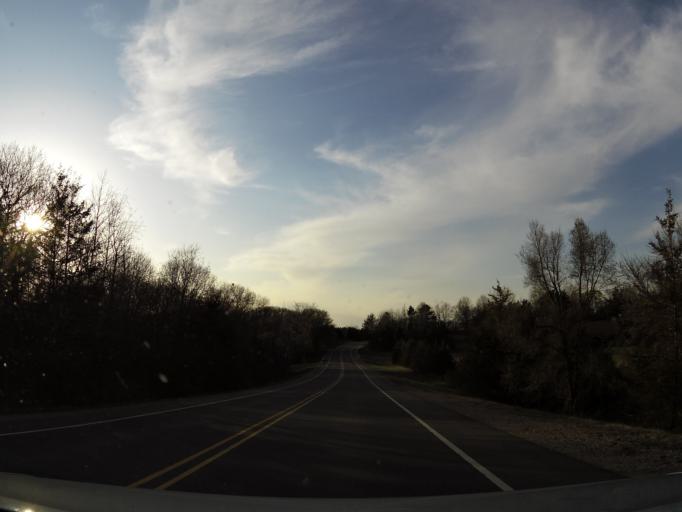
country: US
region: Minnesota
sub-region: Washington County
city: Lake Saint Croix Beach
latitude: 44.9226
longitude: -92.6916
